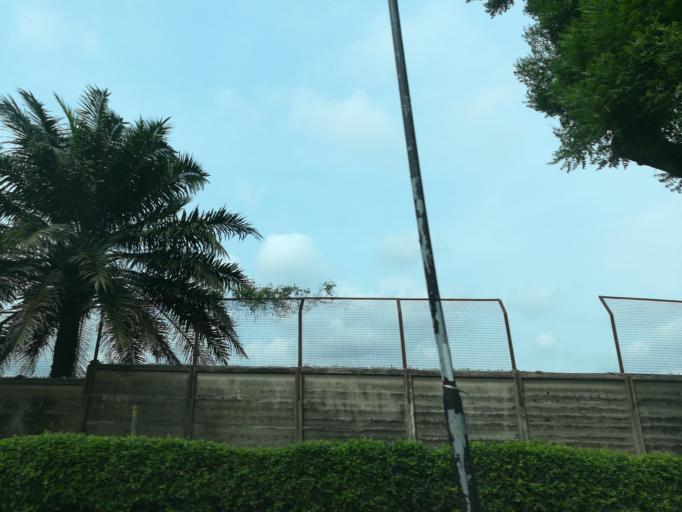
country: NG
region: Lagos
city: Ojota
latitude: 6.6066
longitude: 3.3701
